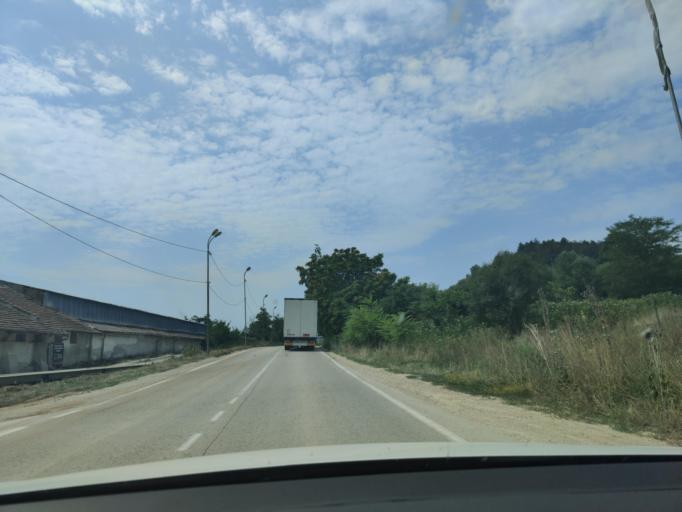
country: BG
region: Vidin
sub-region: Obshtina Dimovo
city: Dimovo
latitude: 43.7507
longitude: 22.7380
